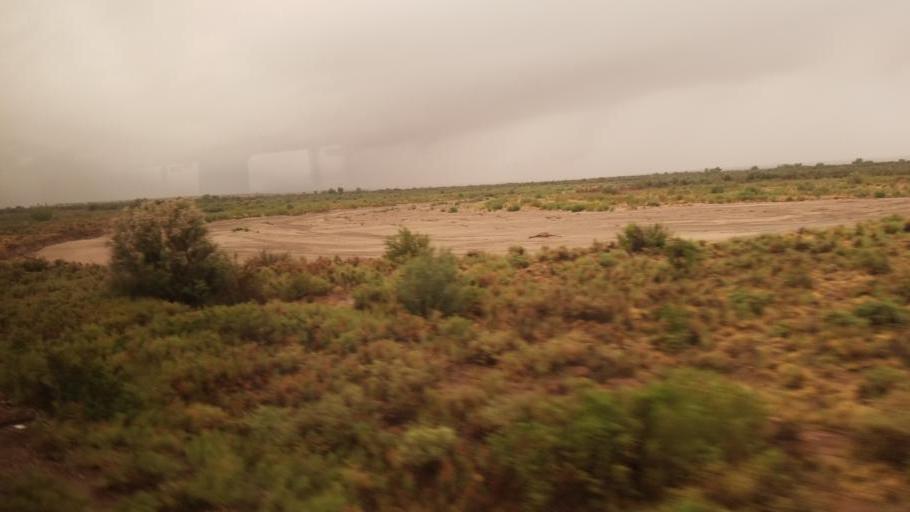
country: US
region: Arizona
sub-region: Navajo County
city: Joseph City
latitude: 34.9674
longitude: -110.4437
